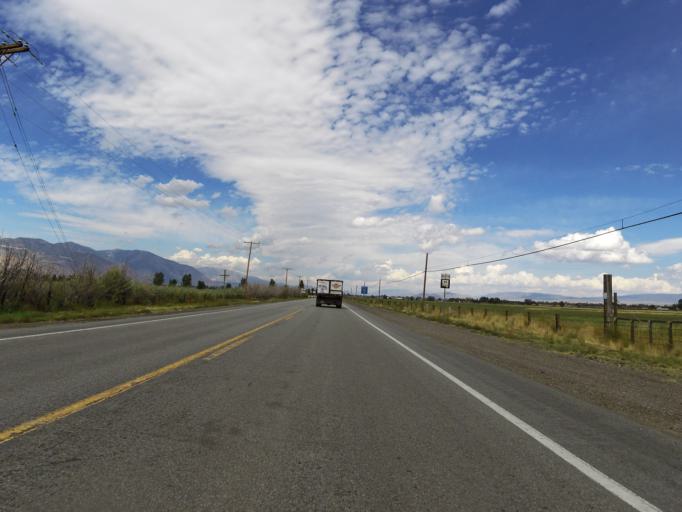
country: US
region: Nevada
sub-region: Douglas County
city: Gardnerville Ranchos
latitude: 38.8679
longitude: -119.7791
